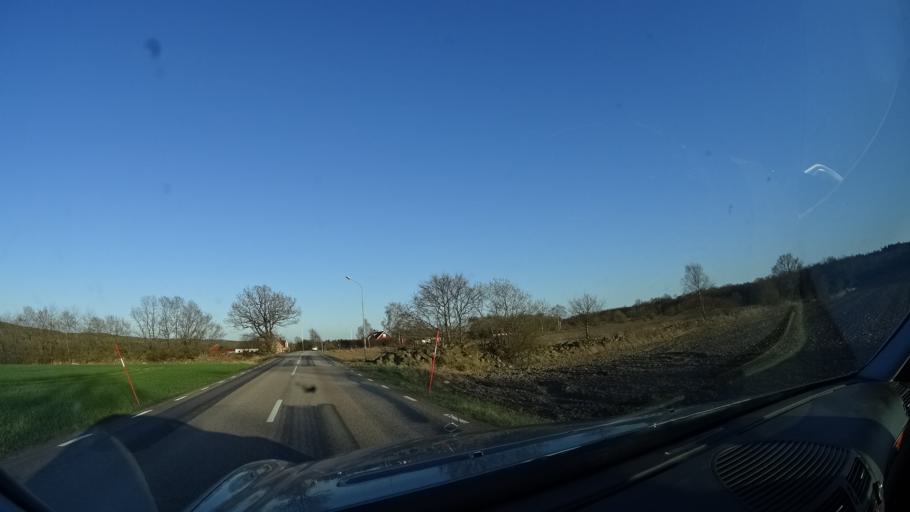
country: SE
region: Skane
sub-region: Svalovs Kommun
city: Kagerod
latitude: 56.0155
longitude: 13.0612
